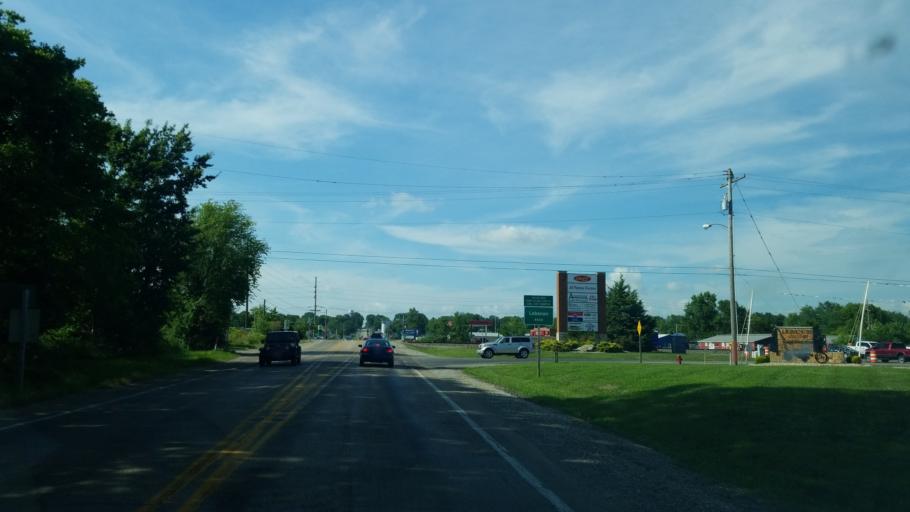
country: US
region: Illinois
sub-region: Saint Clair County
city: Lebanon
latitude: 38.5931
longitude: -89.8077
